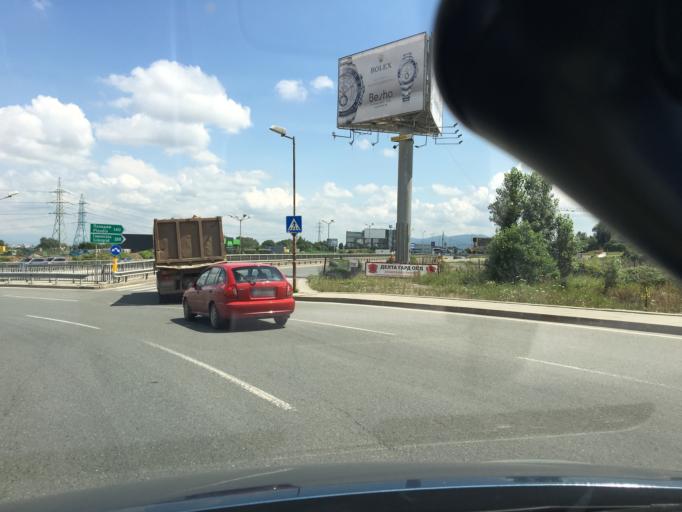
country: BG
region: Sofia-Capital
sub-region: Stolichna Obshtina
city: Sofia
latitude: 42.6414
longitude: 23.3124
